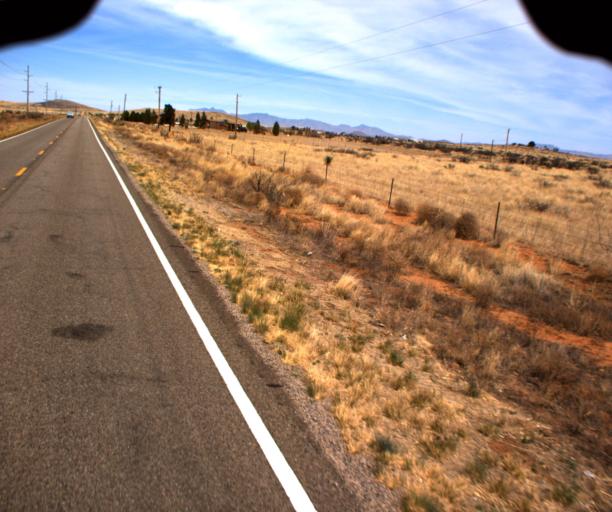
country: US
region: Arizona
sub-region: Cochise County
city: Tombstone
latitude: 31.8699
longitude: -109.6951
